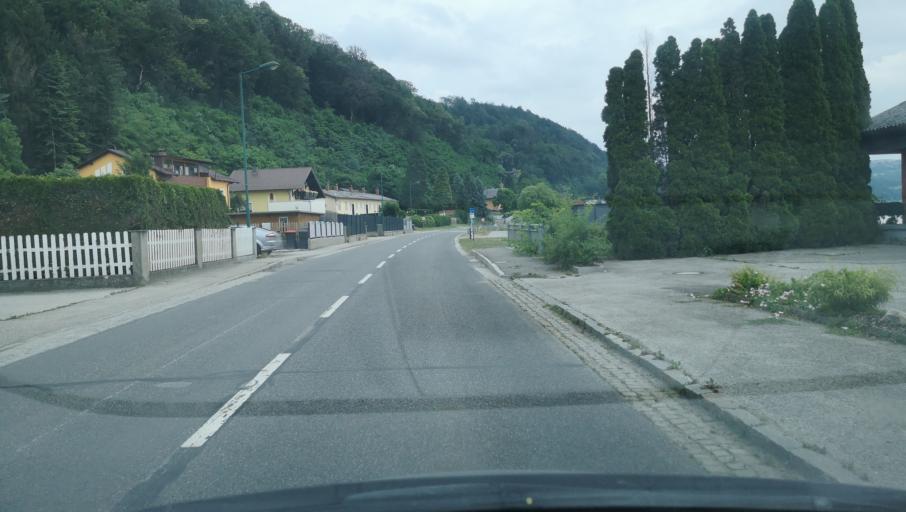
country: AT
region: Lower Austria
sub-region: Politischer Bezirk Melk
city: Ybbs an der Donau
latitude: 48.2000
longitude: 15.1085
